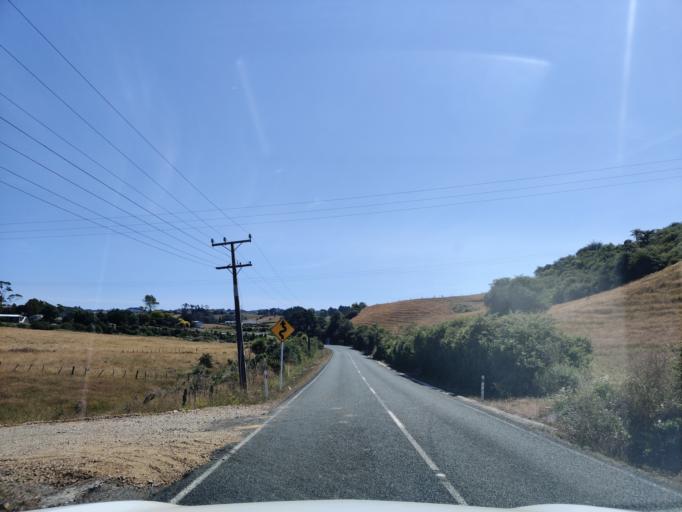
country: NZ
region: Auckland
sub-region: Auckland
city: Red Hill
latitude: -37.0756
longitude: 175.0725
